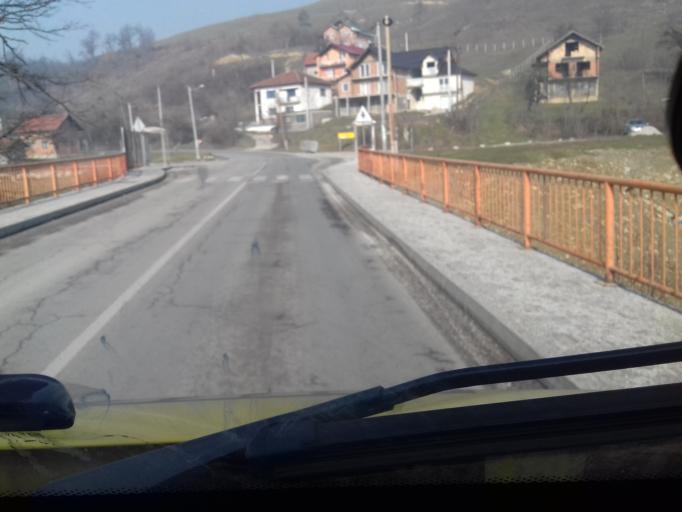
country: BA
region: Federation of Bosnia and Herzegovina
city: Ilijas
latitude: 43.9393
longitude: 18.2799
